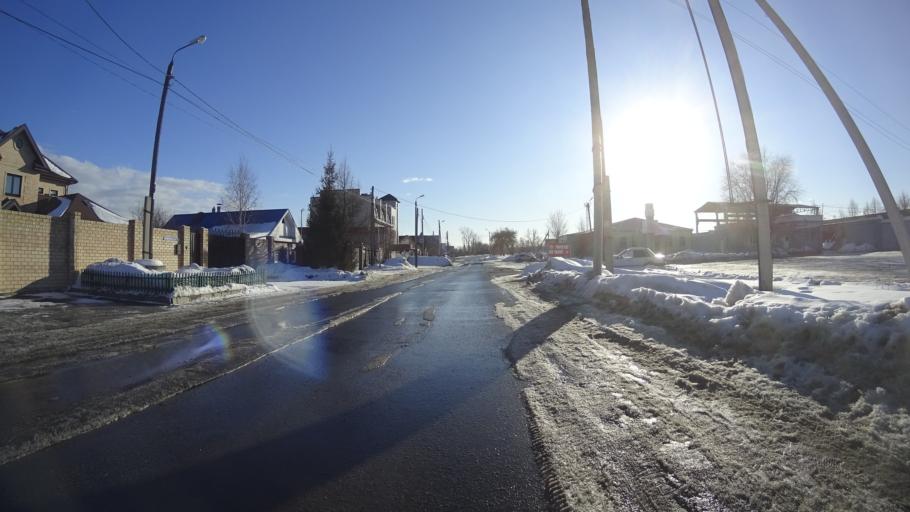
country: RU
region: Chelyabinsk
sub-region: Gorod Chelyabinsk
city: Chelyabinsk
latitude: 55.1508
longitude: 61.3083
